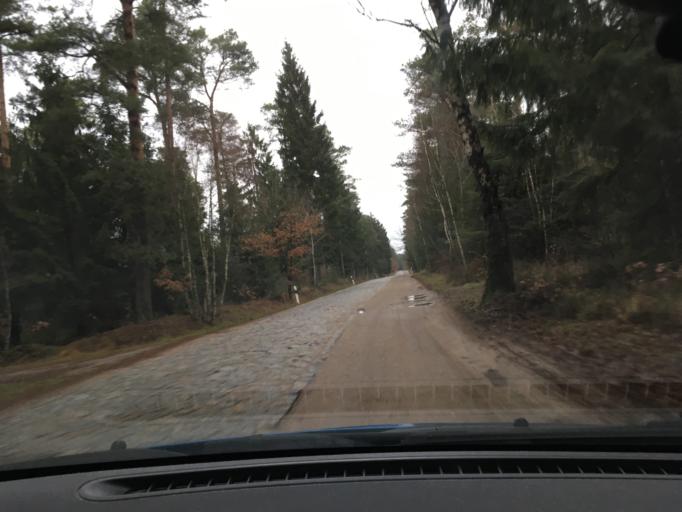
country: DE
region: Schleswig-Holstein
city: Brothen
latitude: 53.4420
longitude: 10.7016
